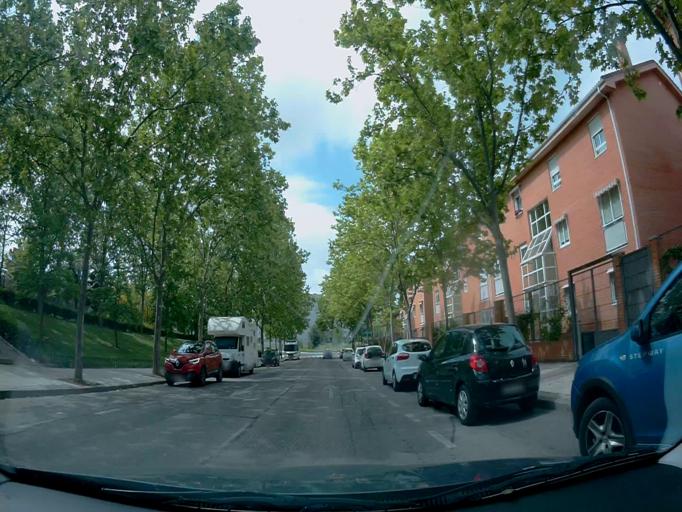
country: ES
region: Madrid
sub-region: Provincia de Madrid
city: Alcorcon
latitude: 40.3352
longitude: -3.8348
